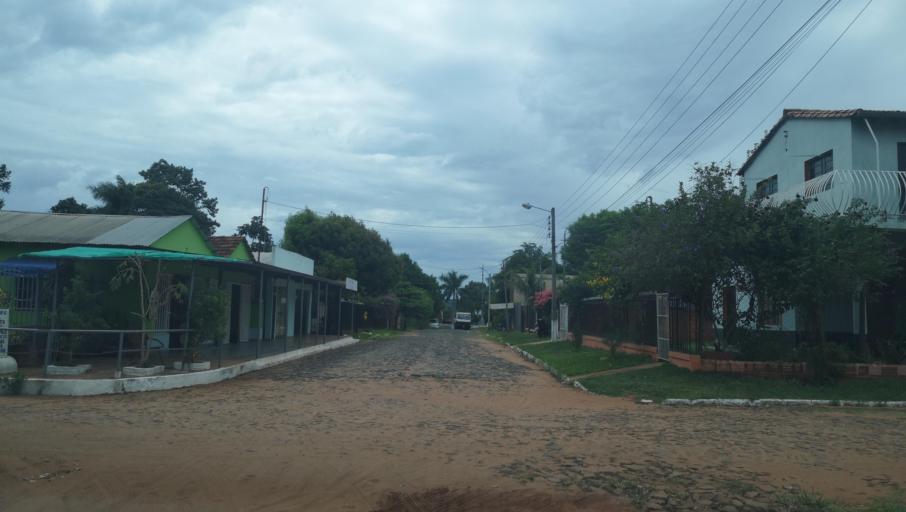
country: PY
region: San Pedro
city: Capiibary
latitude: -24.7283
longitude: -56.0173
